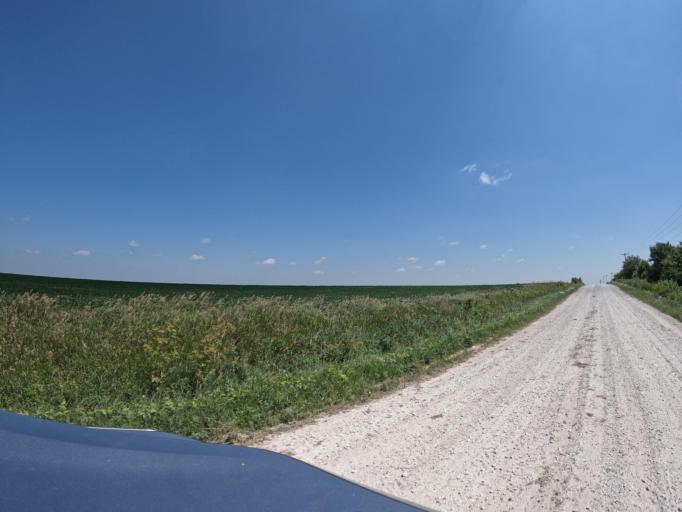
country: US
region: Iowa
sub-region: Keokuk County
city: Sigourney
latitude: 41.2794
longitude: -92.2307
